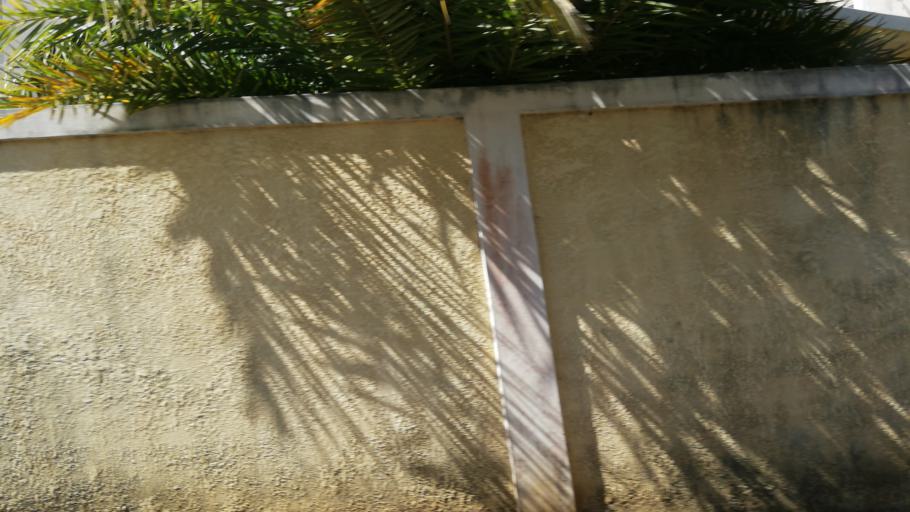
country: MU
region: Plaines Wilhems
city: Ebene
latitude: -20.2356
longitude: 57.4743
